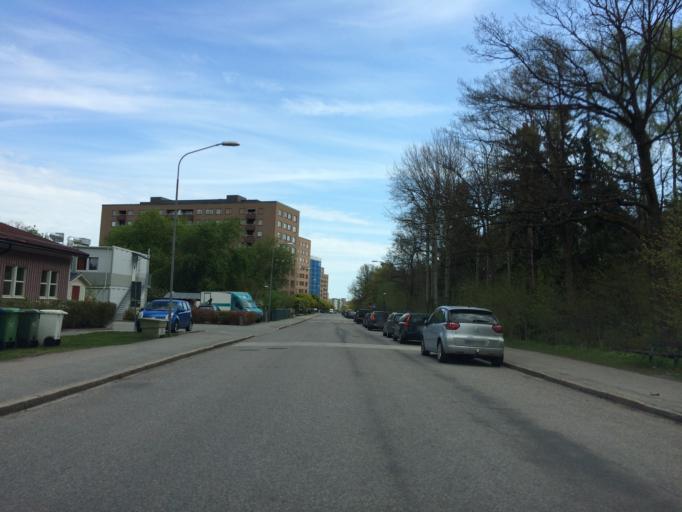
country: SE
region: Stockholm
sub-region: Stockholms Kommun
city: Bromma
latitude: 59.3043
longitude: 17.9668
